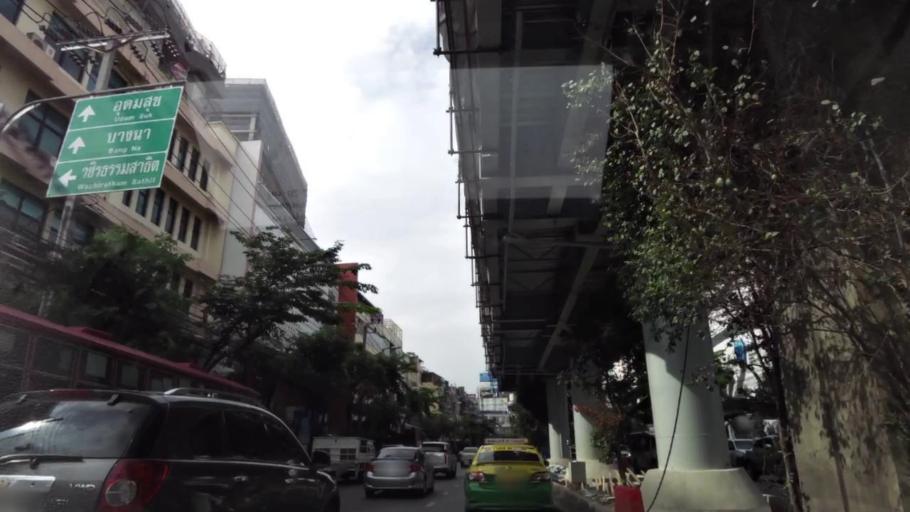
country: TH
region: Bangkok
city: Phra Khanong
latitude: 13.6859
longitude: 100.6104
